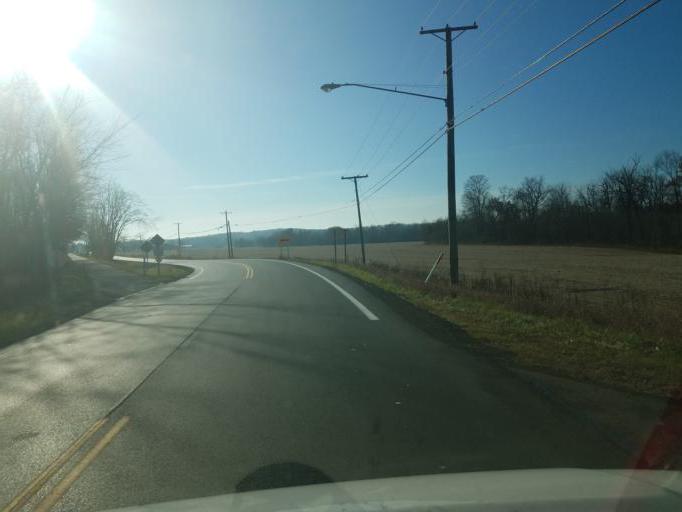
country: US
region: Ohio
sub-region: Sandusky County
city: Bellville
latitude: 40.6390
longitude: -82.5418
